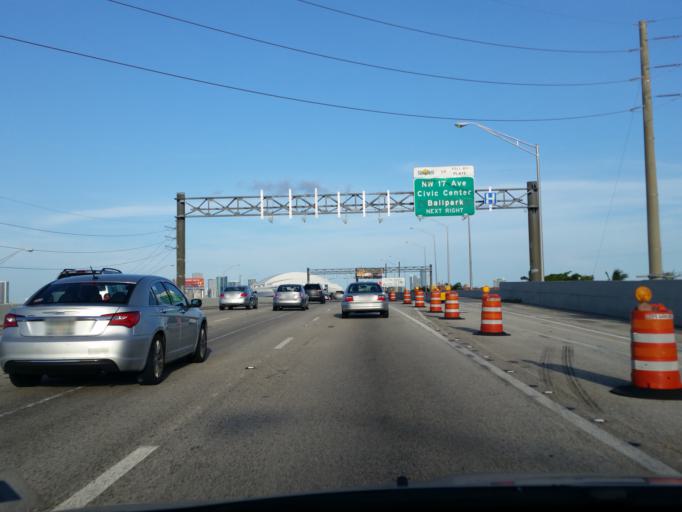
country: US
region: Florida
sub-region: Miami-Dade County
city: Allapattah
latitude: 25.7837
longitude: -80.2343
